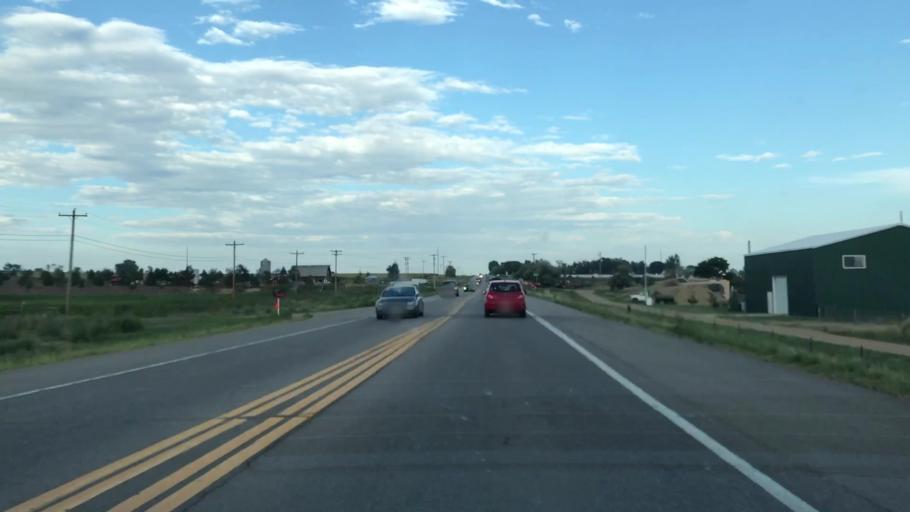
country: US
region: Colorado
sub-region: Weld County
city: Mead
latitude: 40.2034
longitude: -105.0500
